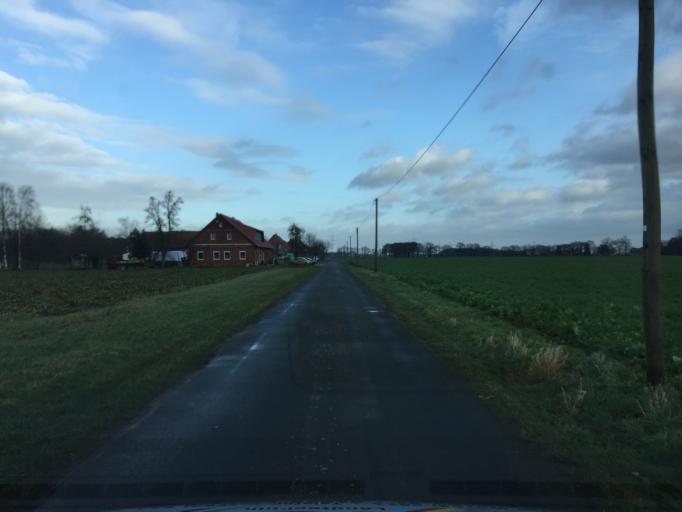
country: DE
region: Lower Saxony
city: Steyerberg
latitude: 52.5352
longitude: 9.0060
